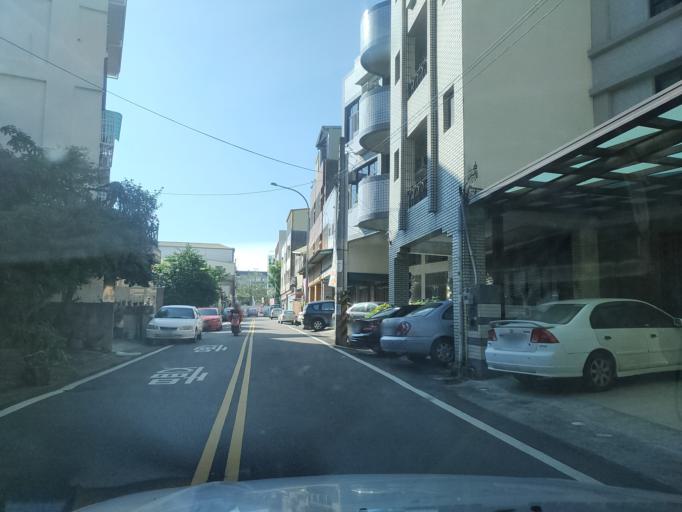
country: TW
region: Taiwan
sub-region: Miaoli
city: Miaoli
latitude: 24.5670
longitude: 120.8253
